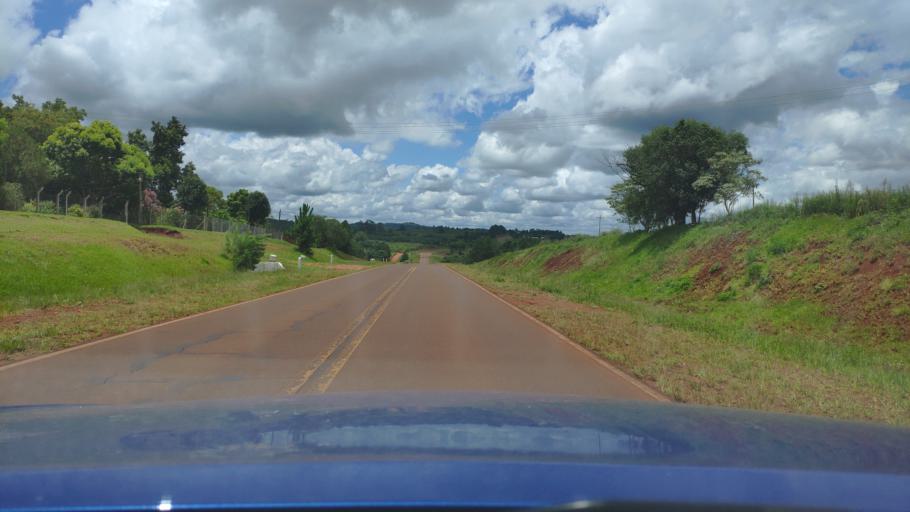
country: AR
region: Misiones
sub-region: Departamento de San Javier
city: San Javier
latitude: -27.8420
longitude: -55.2370
